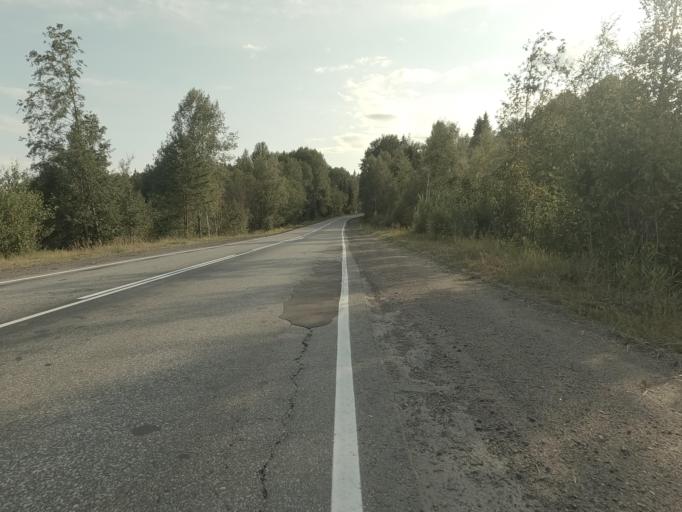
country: RU
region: Leningrad
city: Vyborg
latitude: 60.8445
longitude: 28.8539
